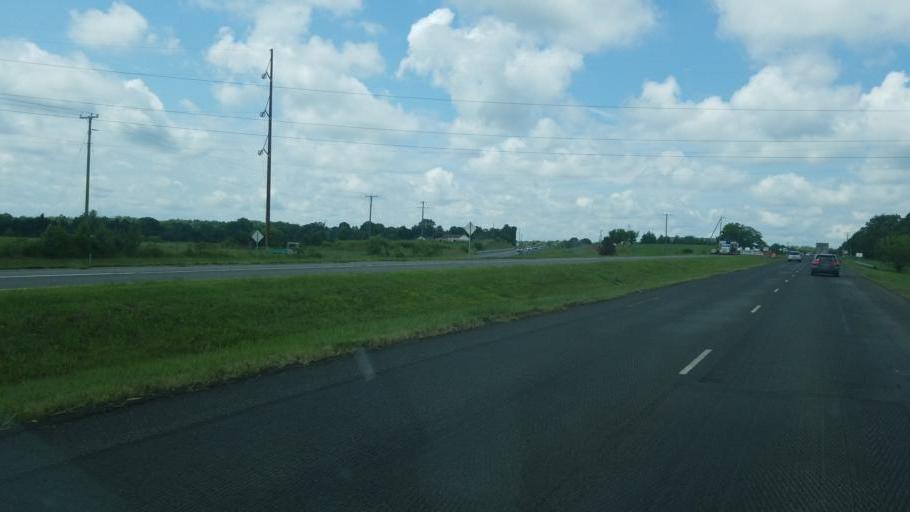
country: US
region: Virginia
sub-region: Fauquier County
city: Bealeton
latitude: 38.6100
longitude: -77.7889
